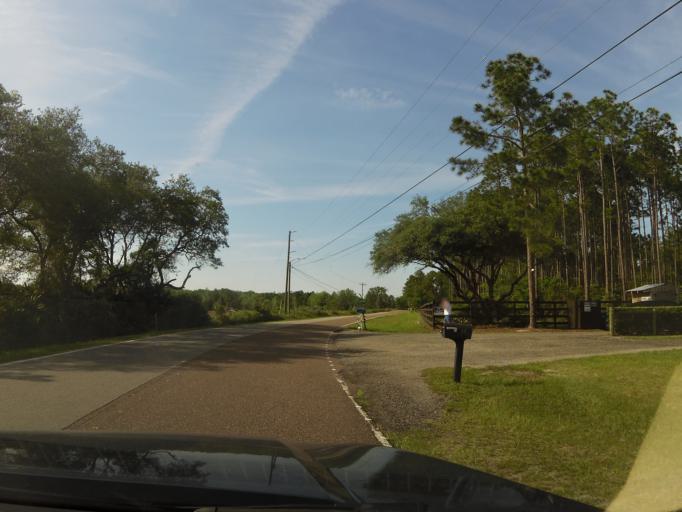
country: US
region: Florida
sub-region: Duval County
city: Atlantic Beach
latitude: 30.4881
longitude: -81.4723
